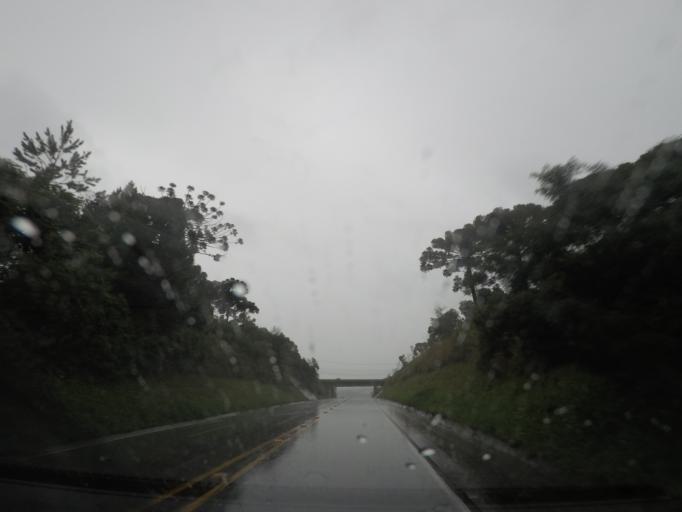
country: BR
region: Parana
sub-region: Almirante Tamandare
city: Almirante Tamandare
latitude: -25.3538
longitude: -49.2931
